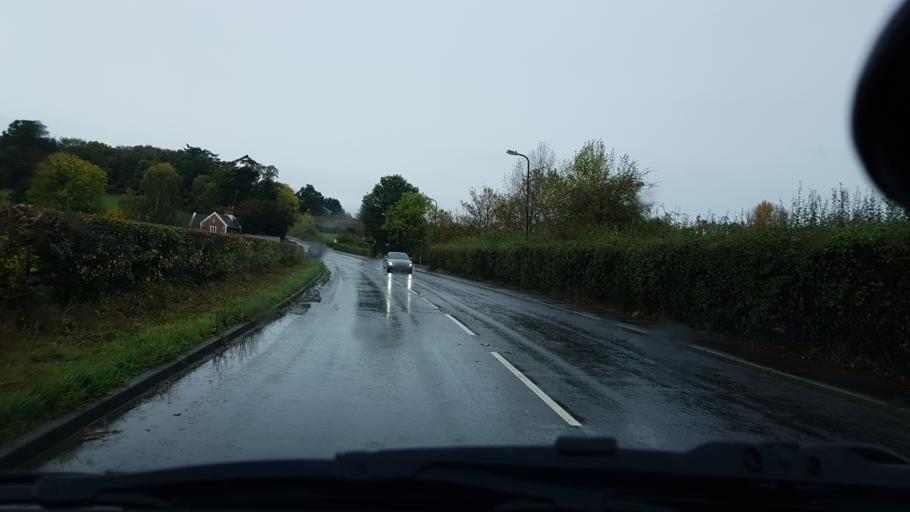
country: GB
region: England
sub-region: Worcestershire
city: Upton upon Severn
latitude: 52.0589
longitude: -2.2220
